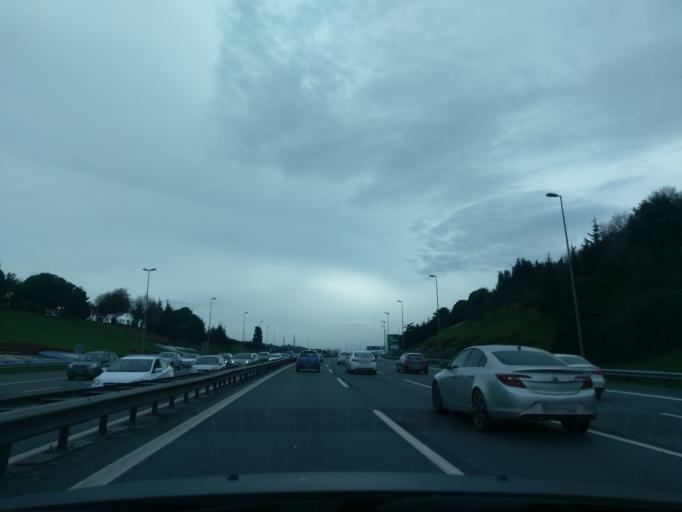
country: TR
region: Istanbul
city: UEskuedar
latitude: 41.0331
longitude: 29.0452
